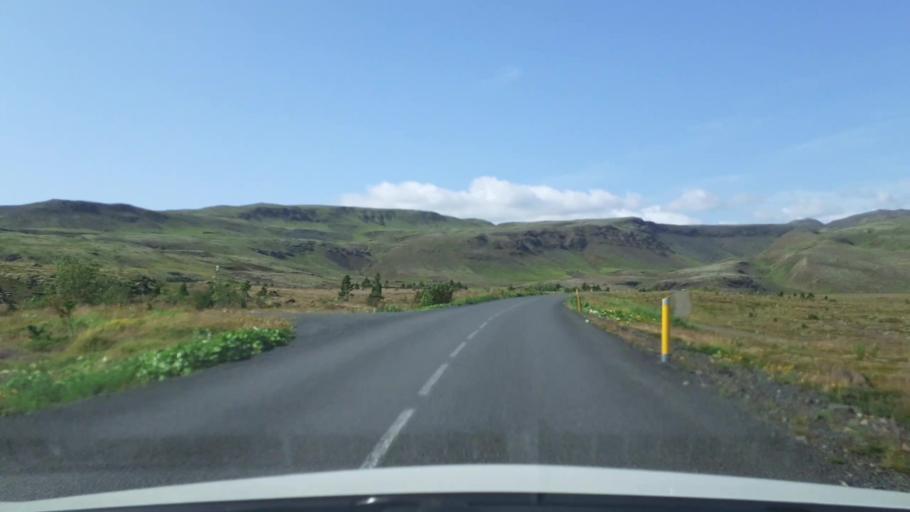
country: IS
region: South
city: Hveragerdi
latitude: 64.0145
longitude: -21.2086
